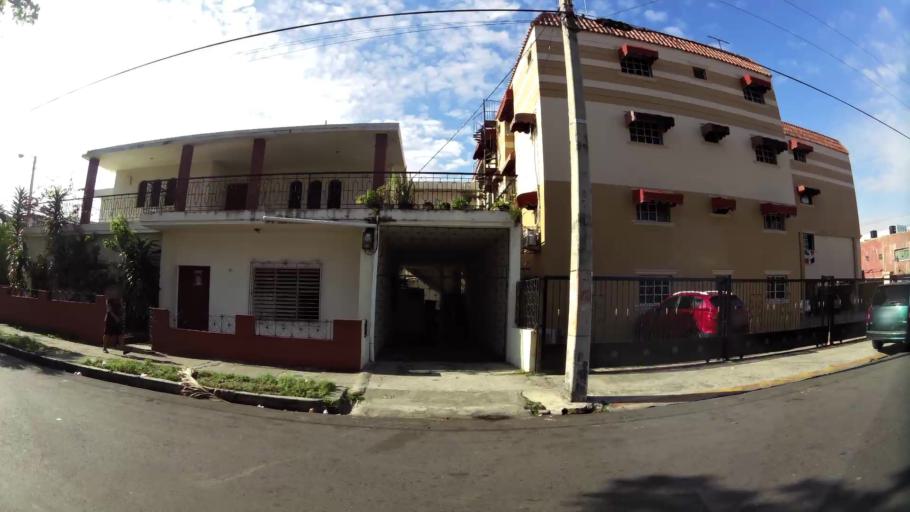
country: DO
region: Santo Domingo
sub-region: Santo Domingo
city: Santo Domingo Este
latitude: 18.4874
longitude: -69.8691
